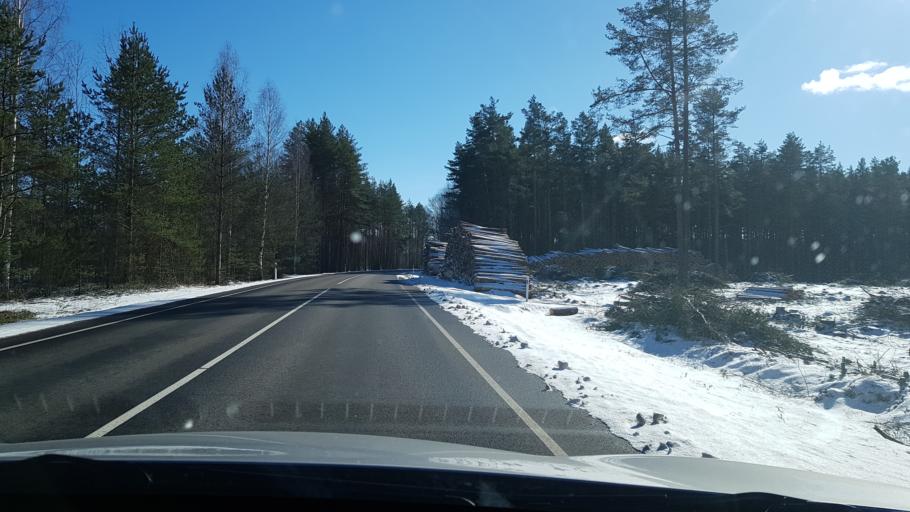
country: EE
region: Polvamaa
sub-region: Raepina vald
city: Rapina
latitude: 57.9920
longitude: 27.5618
